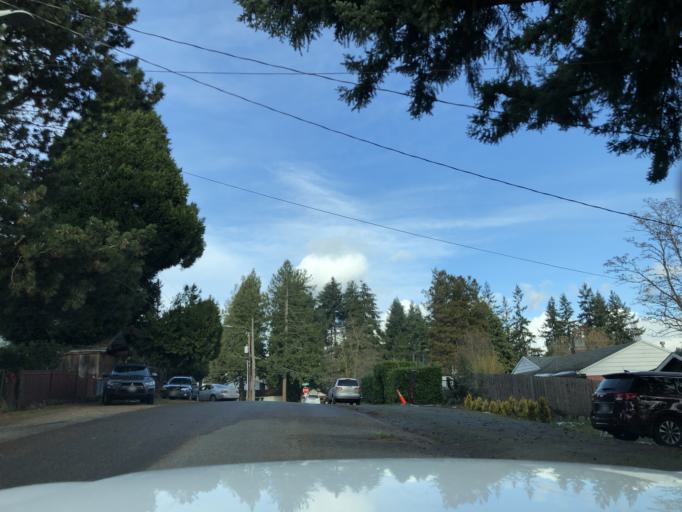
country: US
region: Washington
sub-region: King County
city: Lake Forest Park
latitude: 47.7221
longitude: -122.3005
